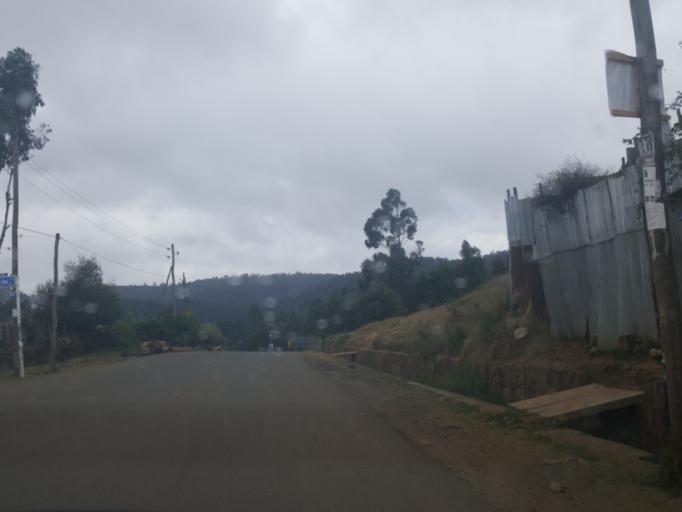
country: ET
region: Adis Abeba
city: Addis Ababa
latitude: 9.0684
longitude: 38.7399
